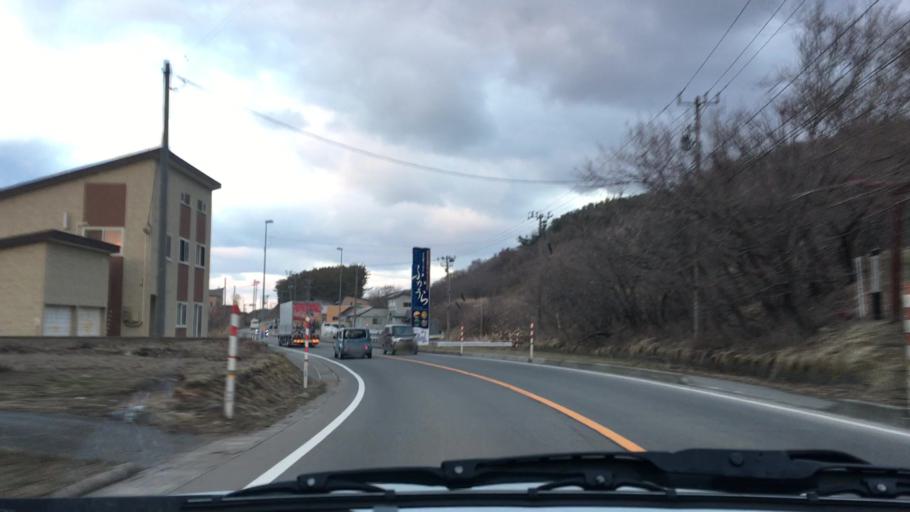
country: JP
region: Aomori
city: Shimokizukuri
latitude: 40.7497
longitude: 140.1434
